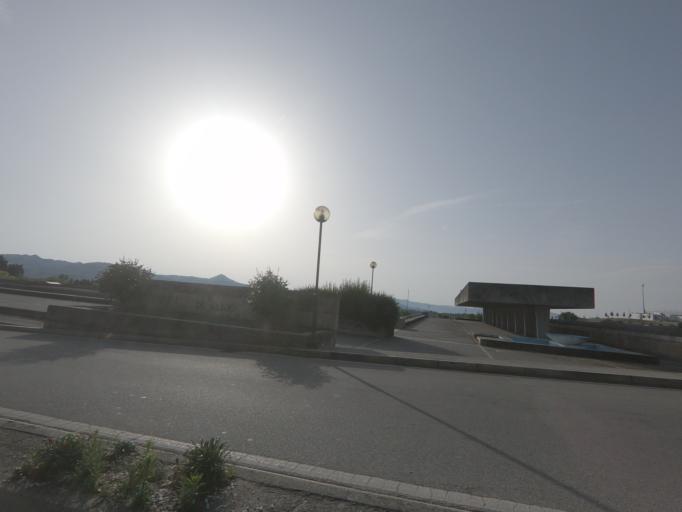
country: PT
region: Vila Real
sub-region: Sabrosa
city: Sabrosa
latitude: 41.2738
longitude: -7.4763
